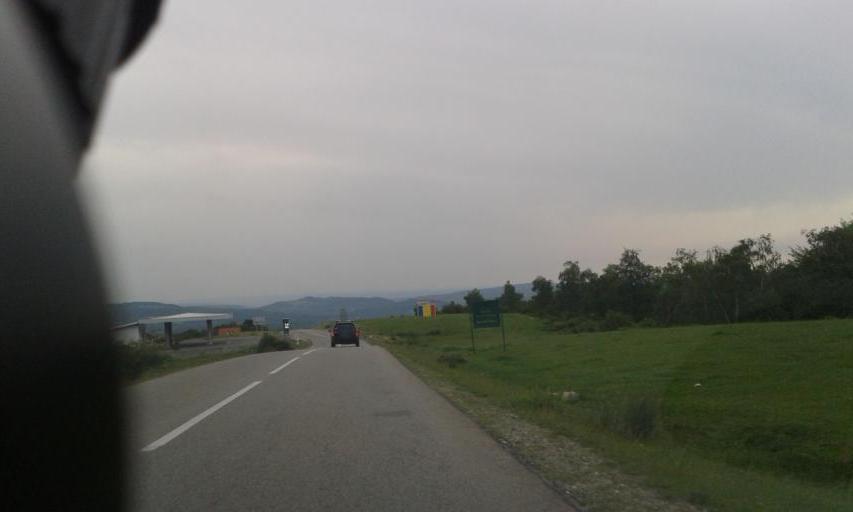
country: RO
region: Gorj
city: Novaci-Straini
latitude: 45.1977
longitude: 23.6889
